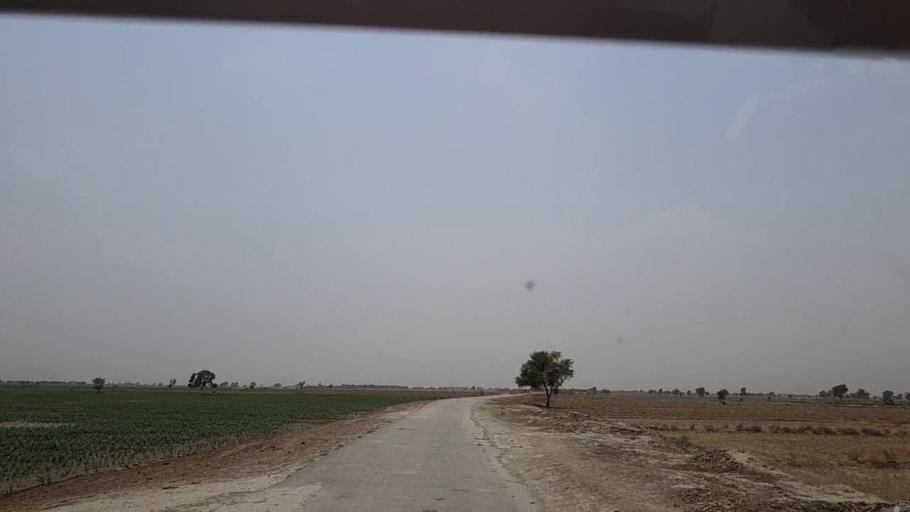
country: PK
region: Sindh
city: Khairpur Nathan Shah
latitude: 27.0179
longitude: 67.6155
